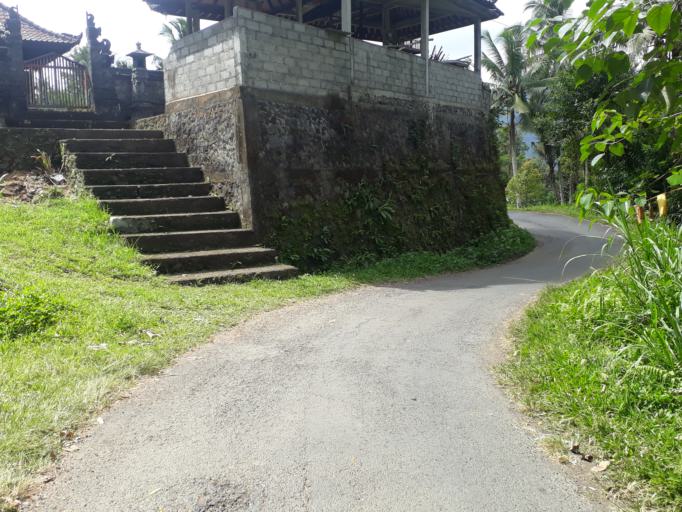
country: ID
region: Bali
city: Banjar Wangsian
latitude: -8.4603
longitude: 115.4343
